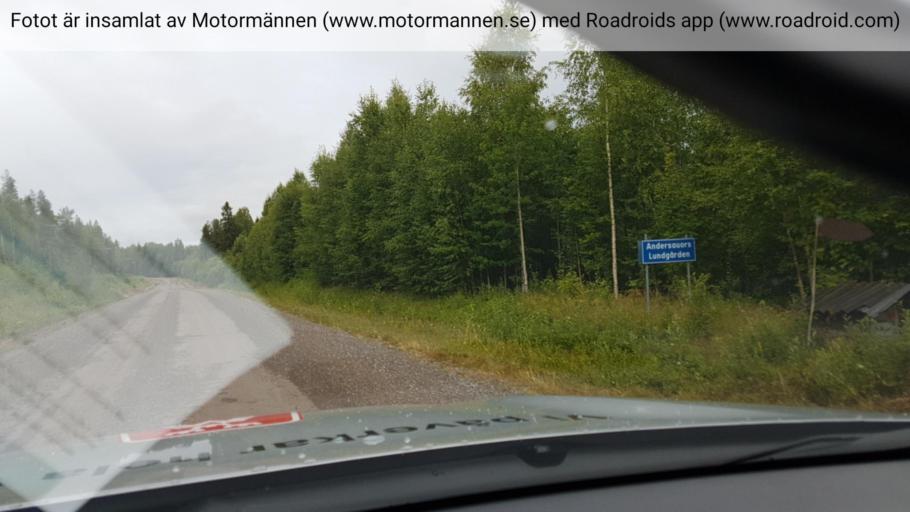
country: SE
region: Norrbotten
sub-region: Alvsbyns Kommun
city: AElvsbyn
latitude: 66.0099
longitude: 21.0946
